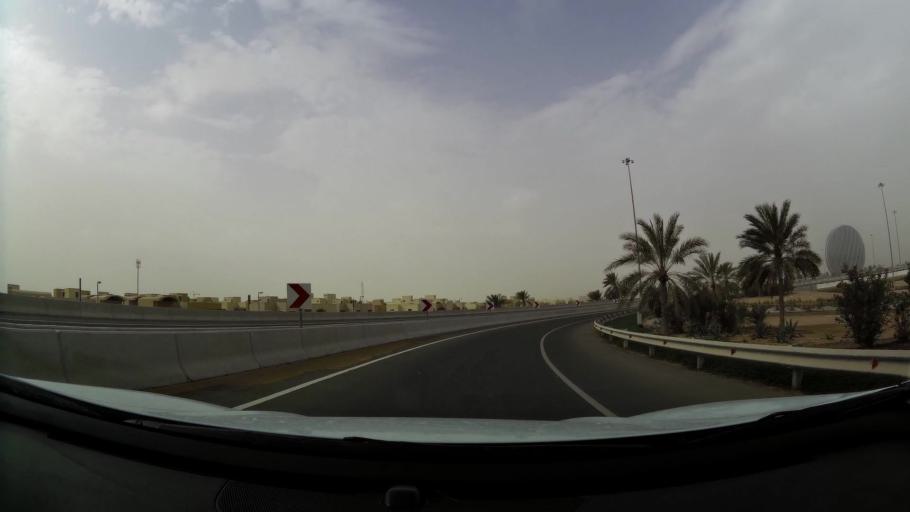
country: AE
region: Abu Dhabi
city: Abu Dhabi
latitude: 24.4391
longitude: 54.5858
